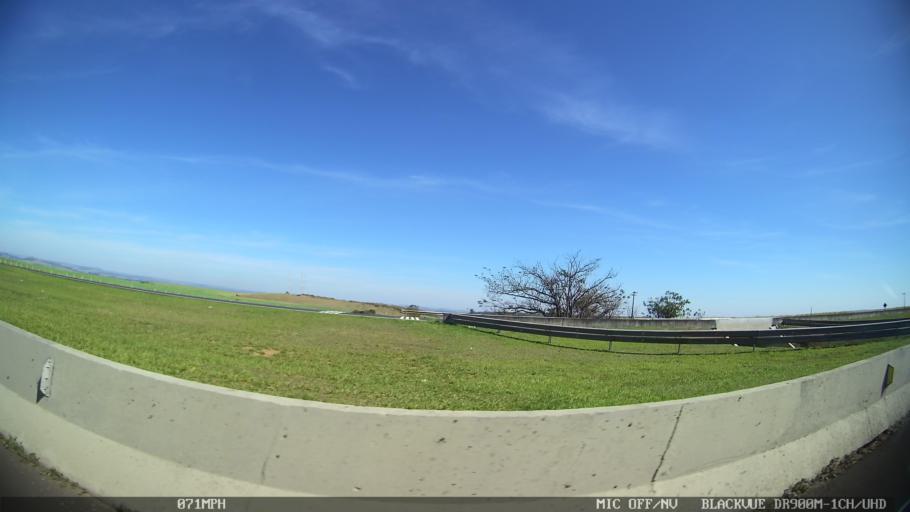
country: BR
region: Sao Paulo
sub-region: Santa Rita Do Passa Quatro
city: Santa Rita do Passa Quatro
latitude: -21.6972
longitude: -47.5971
